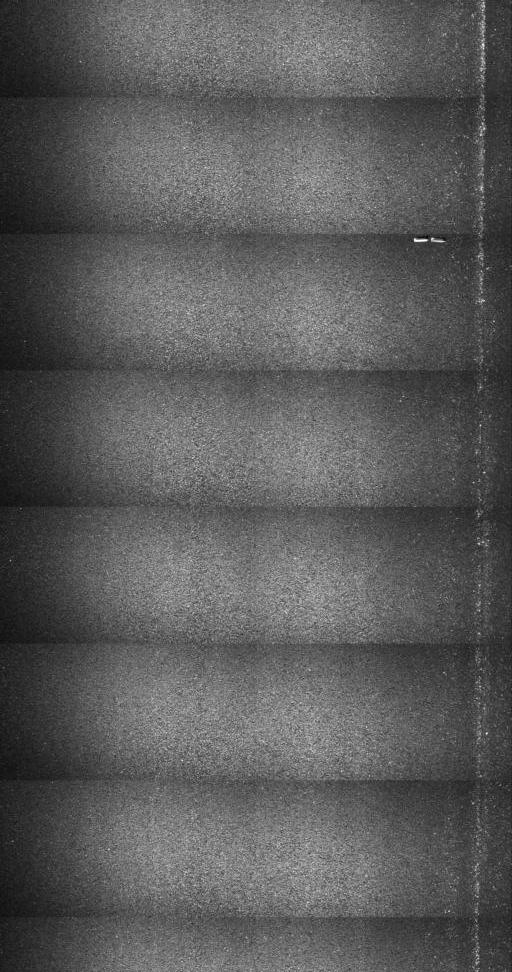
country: US
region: Vermont
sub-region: Franklin County
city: Richford
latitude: 44.8650
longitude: -72.6100
